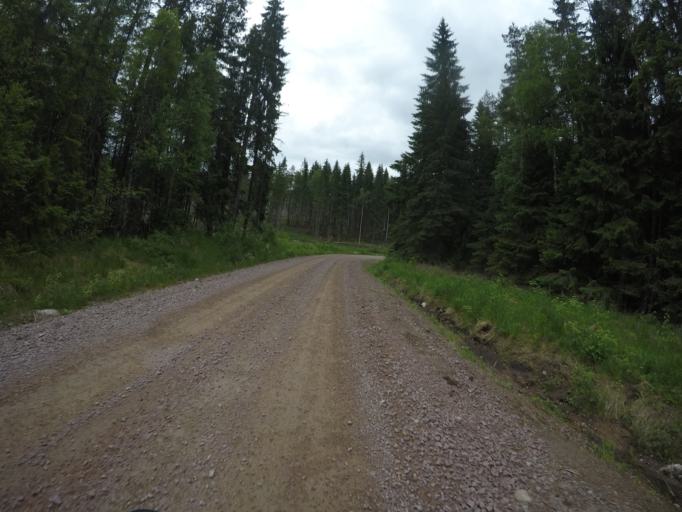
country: SE
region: Dalarna
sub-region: Ludvika Kommun
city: Abborrberget
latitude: 60.1070
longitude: 14.5179
